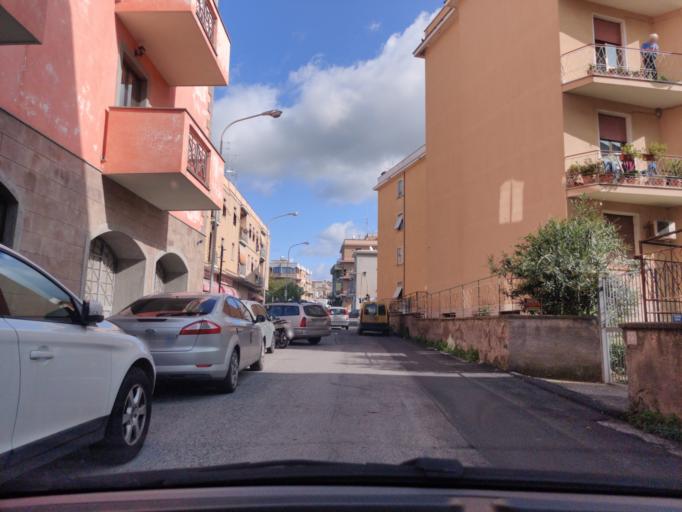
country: IT
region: Latium
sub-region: Citta metropolitana di Roma Capitale
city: Civitavecchia
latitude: 42.0939
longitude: 11.8049
